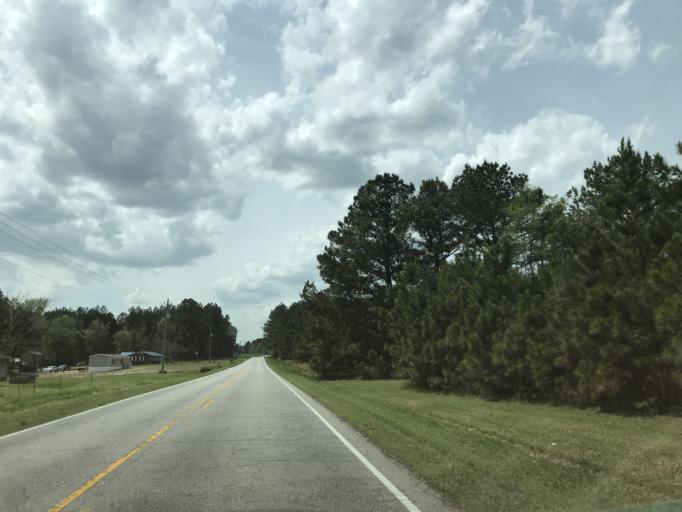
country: US
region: North Carolina
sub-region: Nash County
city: Spring Hope
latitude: 35.9659
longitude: -78.2284
